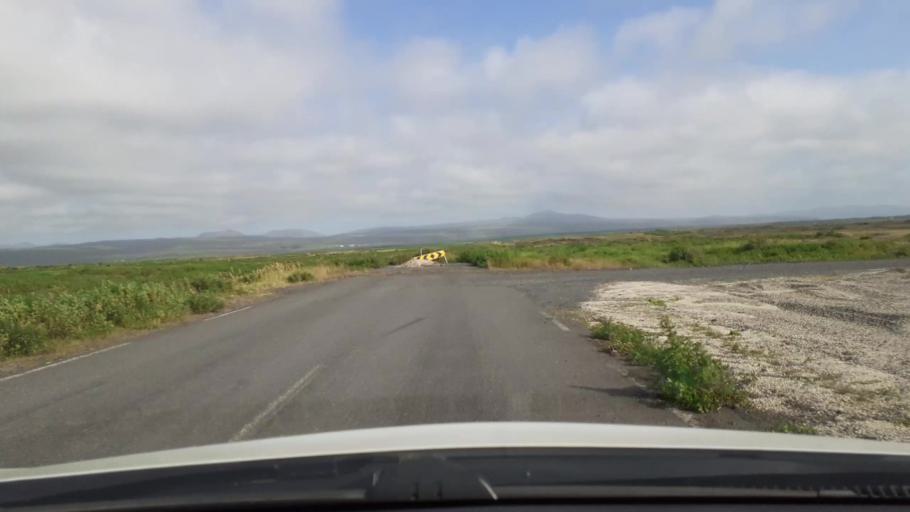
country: IS
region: South
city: THorlakshoefn
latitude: 63.8704
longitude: -21.3822
